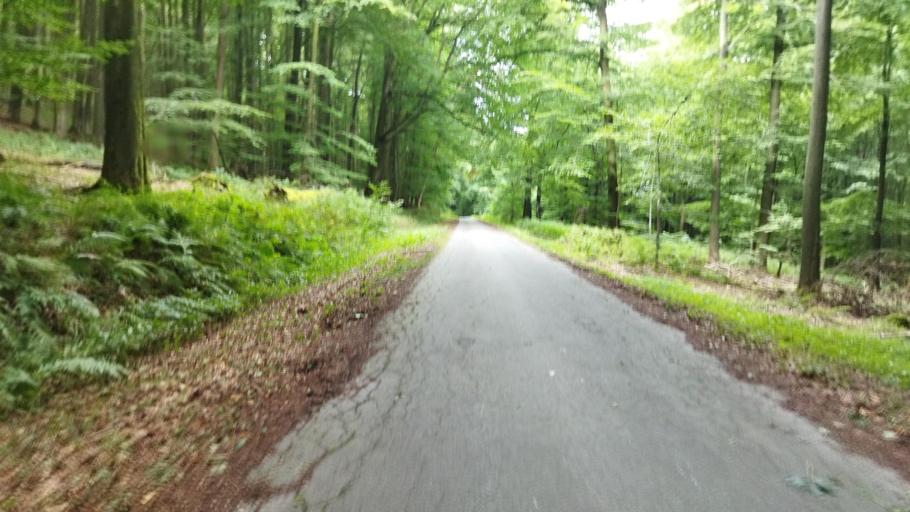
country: DE
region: Lower Saxony
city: Bad Iburg
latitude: 52.1613
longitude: 8.0943
